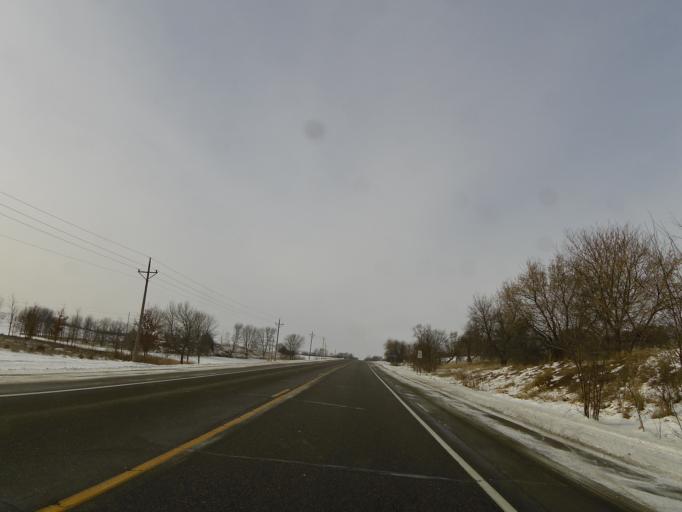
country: US
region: Minnesota
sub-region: Hennepin County
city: Saint Bonifacius
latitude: 44.9053
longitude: -93.7805
